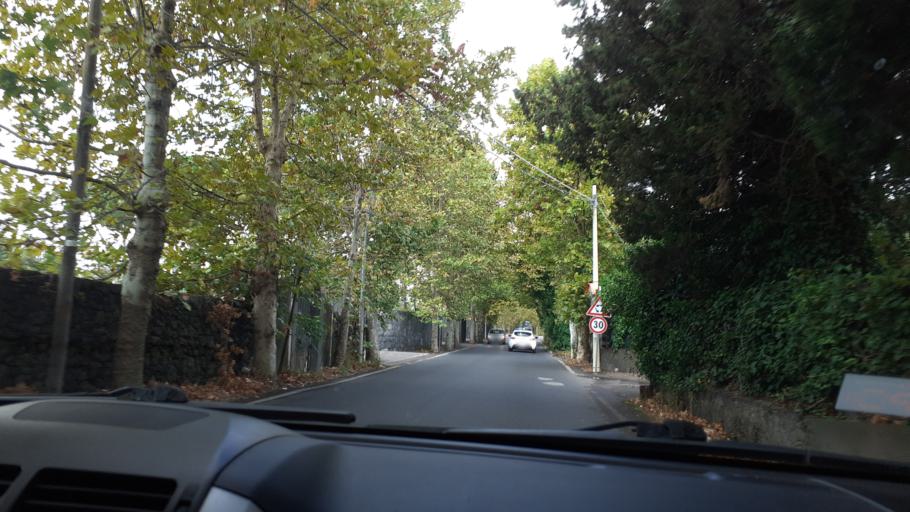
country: IT
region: Sicily
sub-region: Catania
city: San Gregorio di Catania
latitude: 37.5702
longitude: 15.1019
